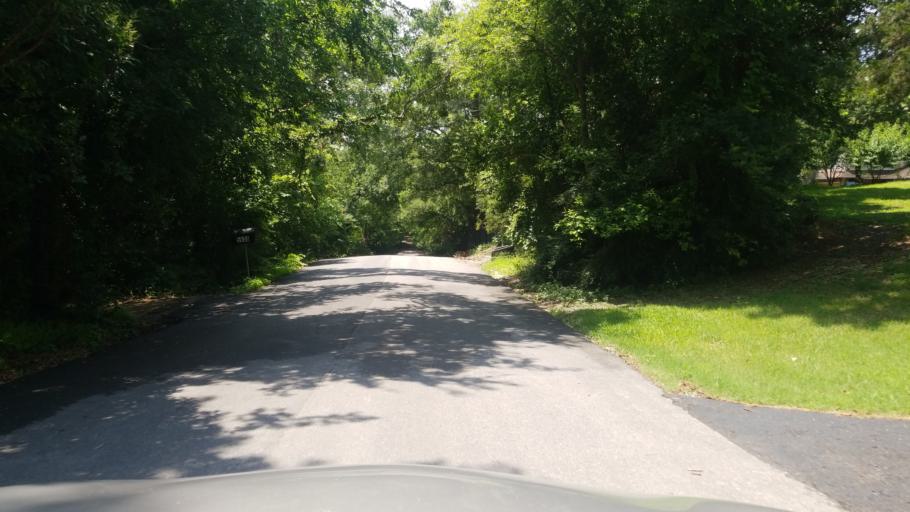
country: US
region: Texas
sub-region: Dallas County
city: Duncanville
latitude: 32.6777
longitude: -96.9215
